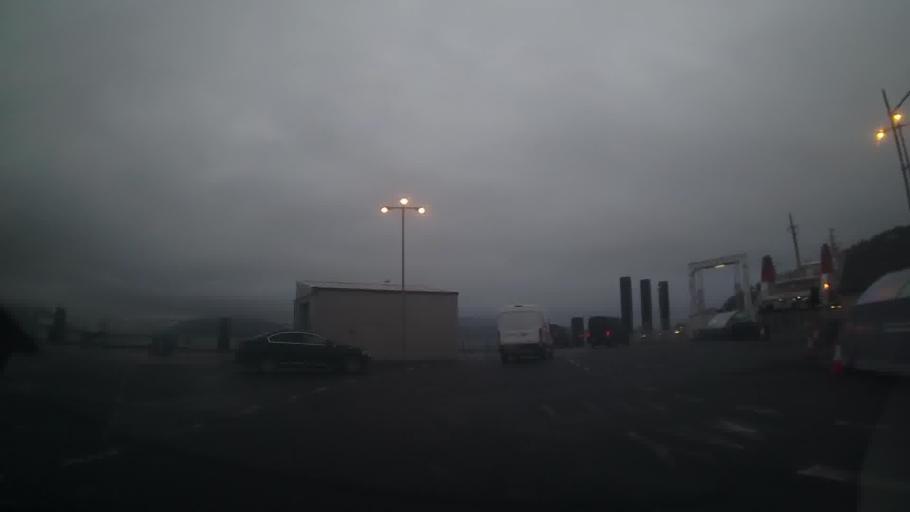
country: GB
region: Scotland
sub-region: Argyll and Bute
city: Rothesay
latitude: 55.8390
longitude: -5.0546
